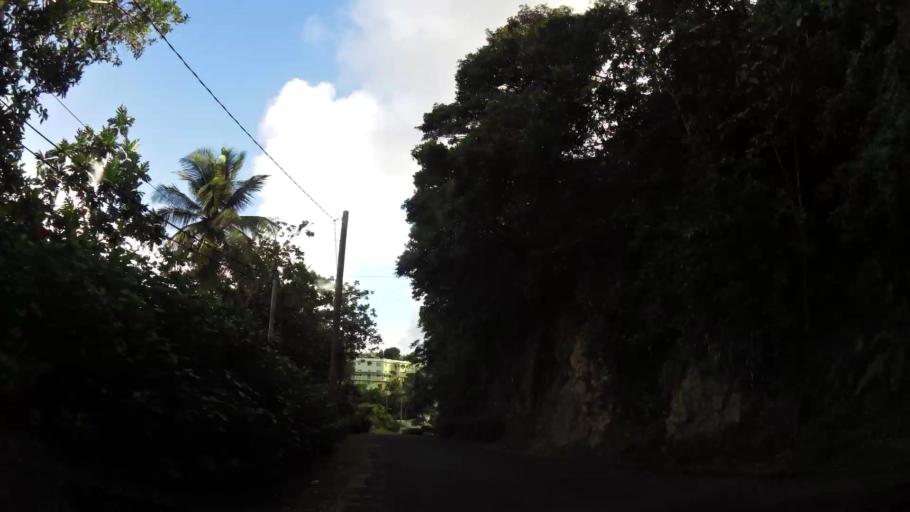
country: DM
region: Saint Andrew
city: Calibishie
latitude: 15.5941
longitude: -61.3872
